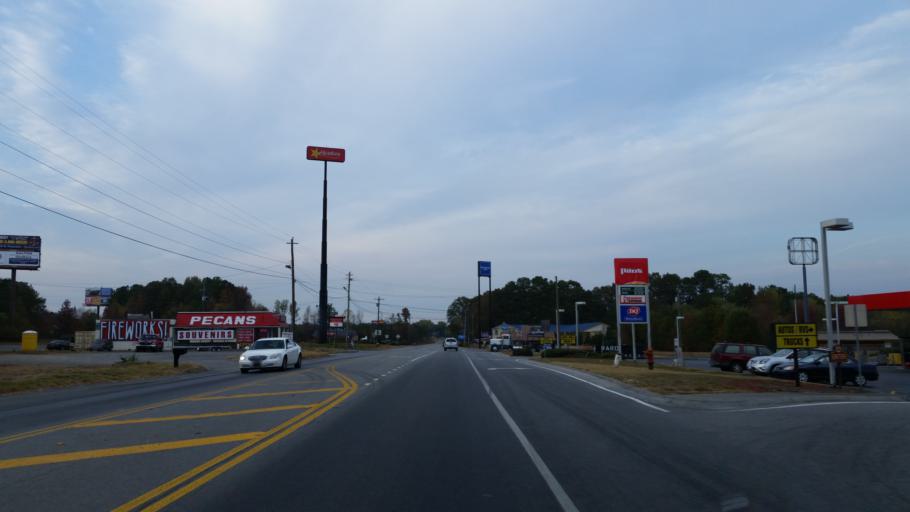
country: US
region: Georgia
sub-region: Gordon County
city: Calhoun
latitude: 34.5583
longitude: -84.9363
